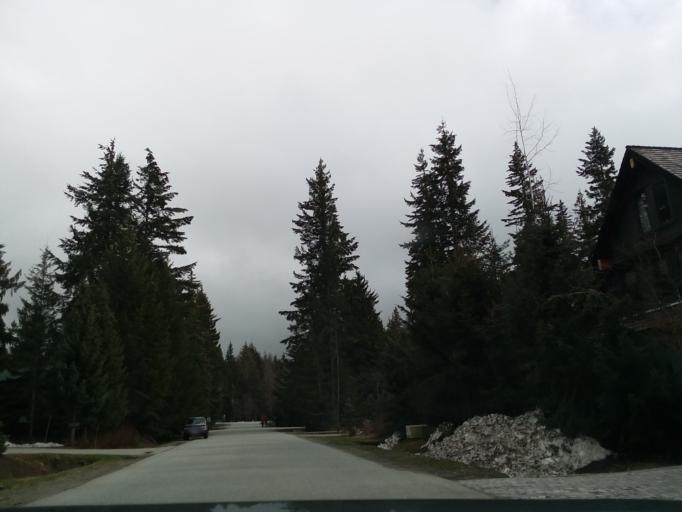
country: CA
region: British Columbia
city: Whistler
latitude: 50.1279
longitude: -122.9686
